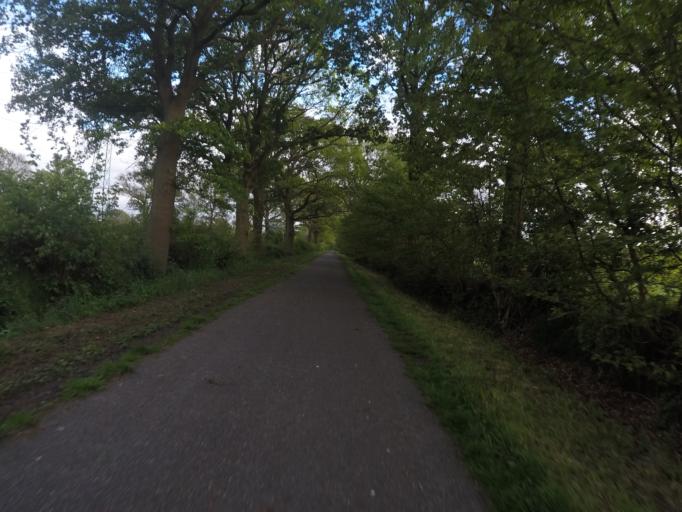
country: DE
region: Schleswig-Holstein
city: Bonningstedt
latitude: 53.6823
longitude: 9.9282
